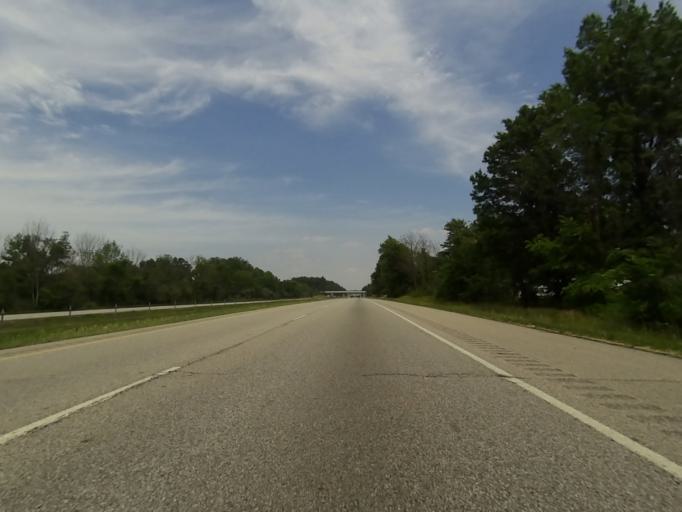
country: US
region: Ohio
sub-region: Mahoning County
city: Craig Beach
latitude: 41.0998
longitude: -81.0089
